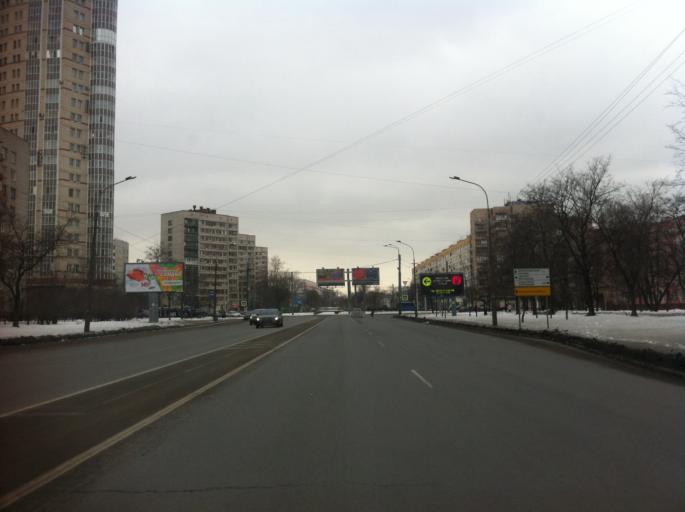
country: RU
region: St.-Petersburg
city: Dachnoye
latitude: 59.8435
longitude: 30.2520
